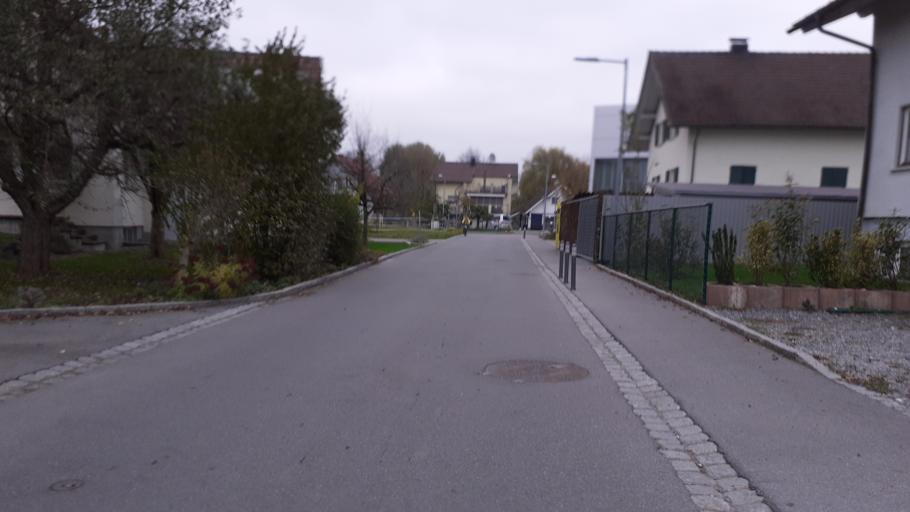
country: AT
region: Vorarlberg
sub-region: Politischer Bezirk Dornbirn
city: Lustenau
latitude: 47.4252
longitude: 9.6687
